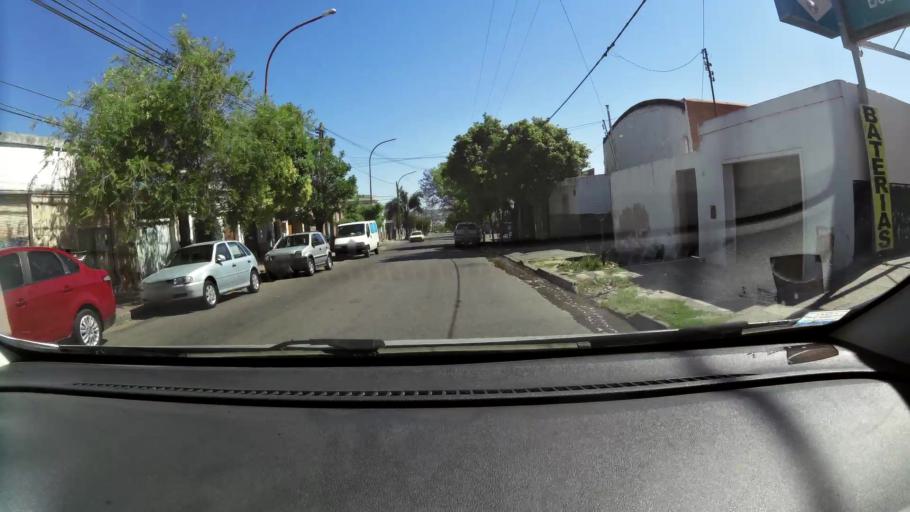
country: AR
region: Cordoba
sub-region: Departamento de Capital
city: Cordoba
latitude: -31.4308
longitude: -64.1515
